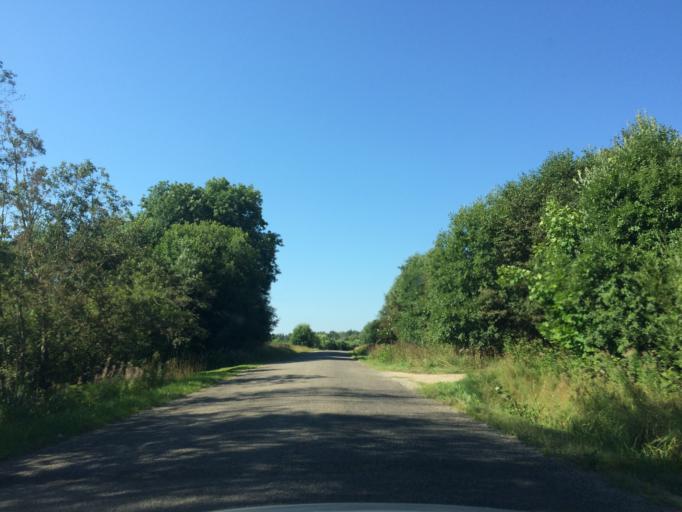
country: LV
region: Rezekne
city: Rezekne
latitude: 56.4969
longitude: 27.2861
